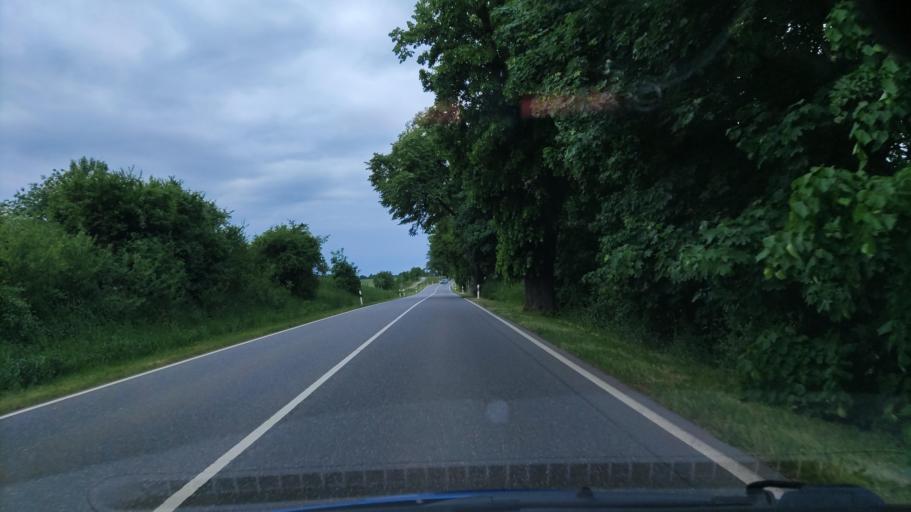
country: DE
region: Mecklenburg-Vorpommern
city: Plau am See
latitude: 53.4570
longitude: 12.2389
